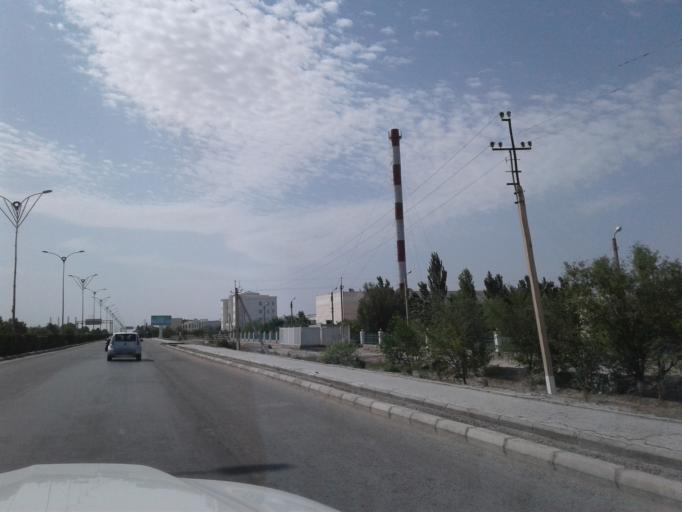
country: TM
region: Dasoguz
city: Dasoguz
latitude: 41.8331
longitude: 59.9364
